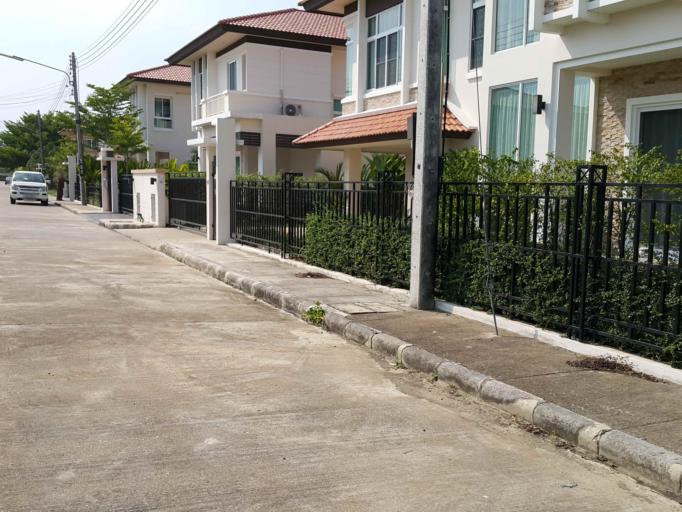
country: TH
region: Chiang Mai
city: Saraphi
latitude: 18.7554
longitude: 99.0426
